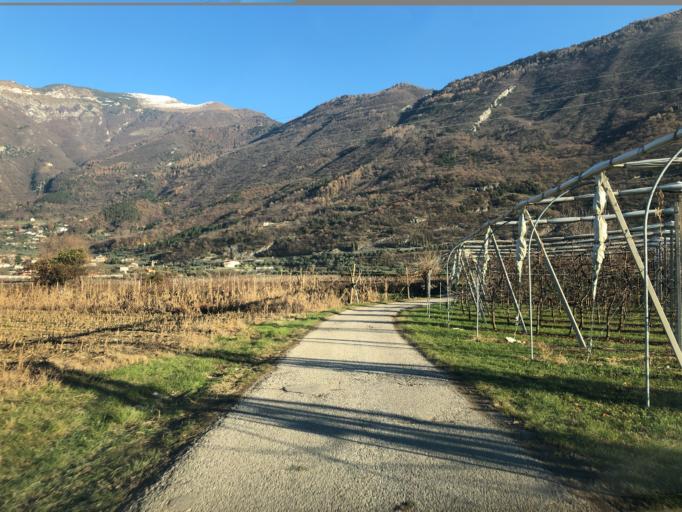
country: IT
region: Trentino-Alto Adige
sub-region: Provincia di Trento
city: Arco
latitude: 45.9040
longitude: 10.8905
